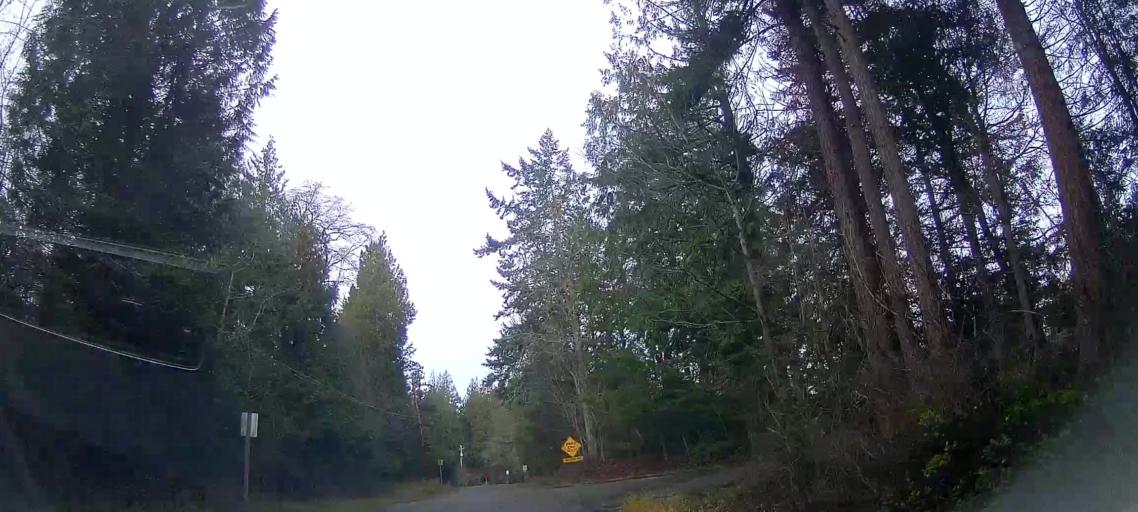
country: US
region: Washington
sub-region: Skagit County
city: Anacortes
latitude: 48.5792
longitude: -122.5527
